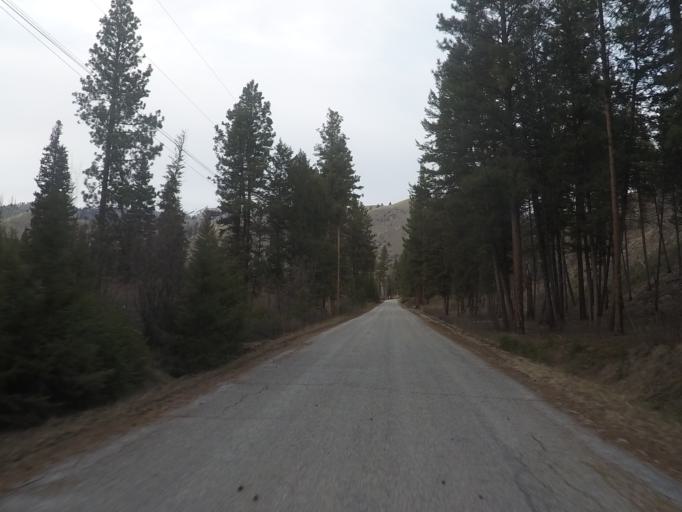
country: US
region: Montana
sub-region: Ravalli County
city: Hamilton
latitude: 45.8509
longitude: -114.0322
